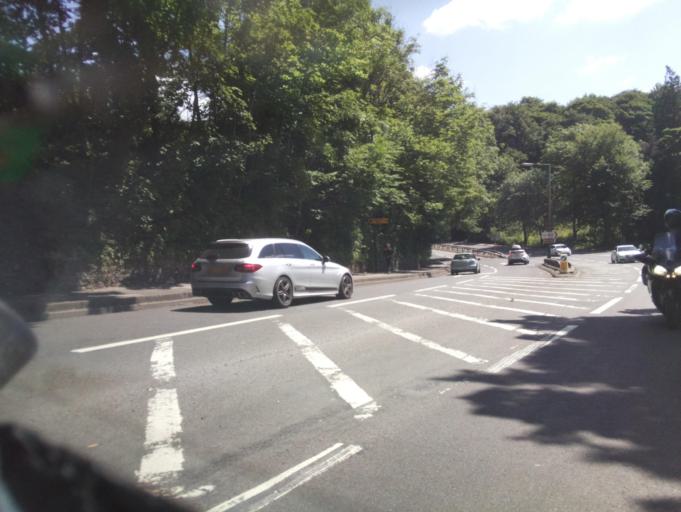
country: GB
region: England
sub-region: Derbyshire
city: Buxton
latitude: 53.2480
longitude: -1.9090
